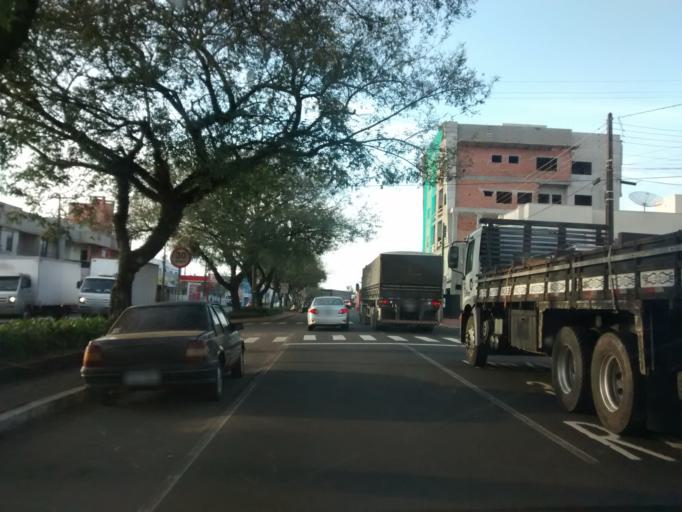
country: BR
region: Parana
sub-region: Francisco Beltrao
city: Francisco Beltrao
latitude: -26.1470
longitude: -53.0248
